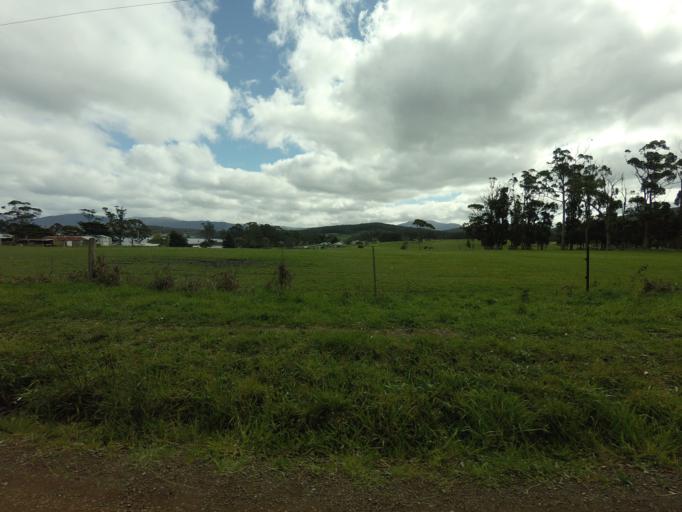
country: AU
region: Tasmania
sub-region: Huon Valley
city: Geeveston
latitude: -43.4356
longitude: 146.9862
